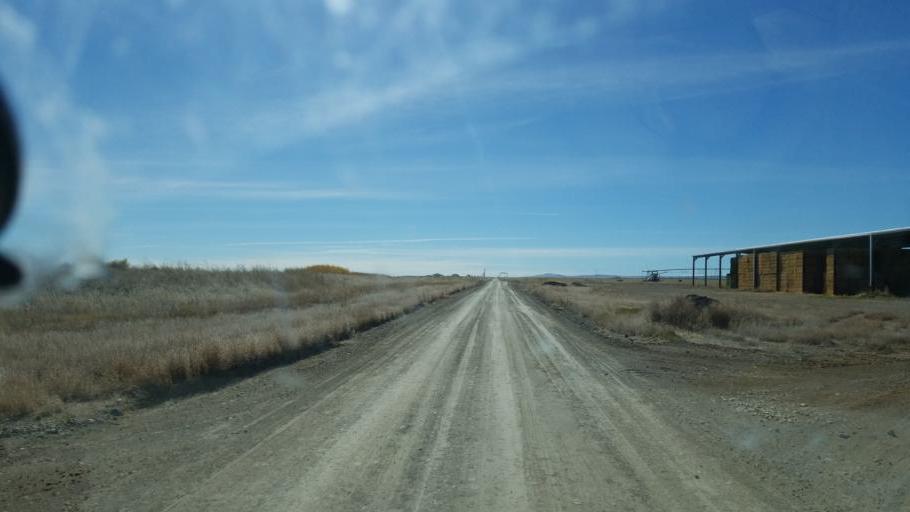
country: US
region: Colorado
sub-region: Rio Grande County
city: Monte Vista
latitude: 37.4081
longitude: -106.1304
